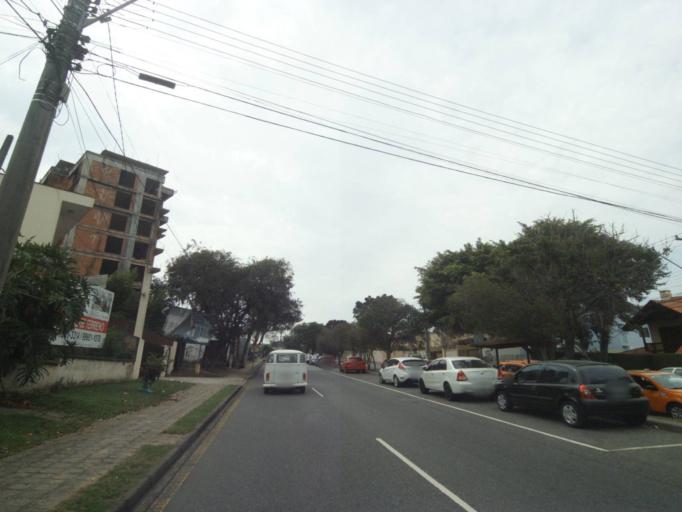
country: BR
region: Parana
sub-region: Curitiba
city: Curitiba
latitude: -25.4524
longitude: -49.3034
